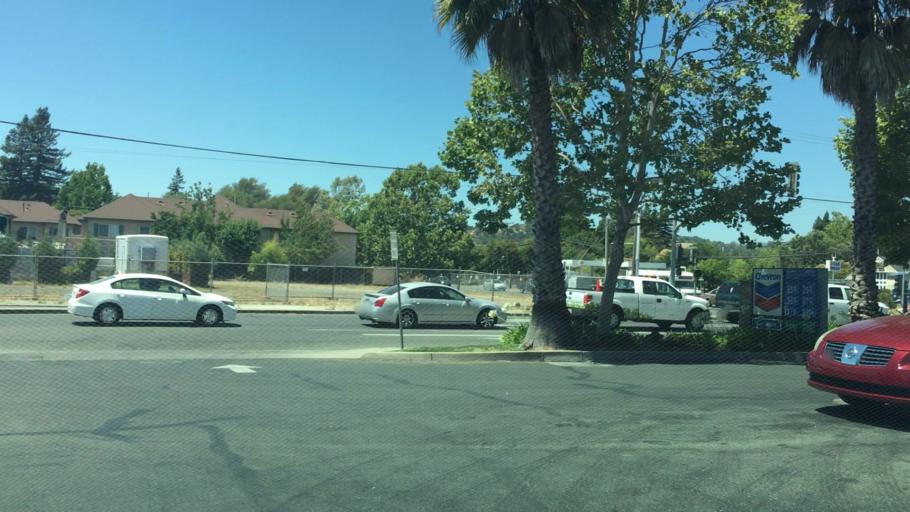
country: US
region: California
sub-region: Napa County
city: Napa
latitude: 38.2815
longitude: -122.2933
